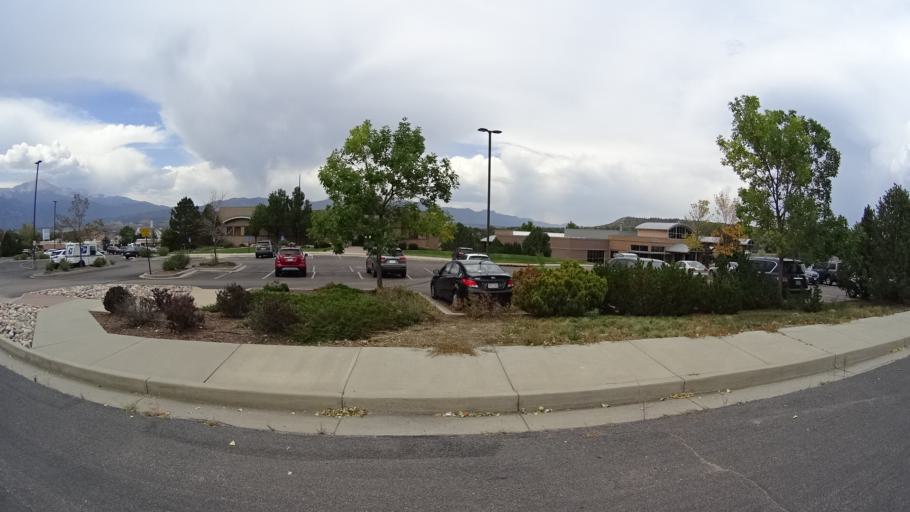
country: US
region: Colorado
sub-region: El Paso County
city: Colorado Springs
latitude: 38.8717
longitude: -104.7914
